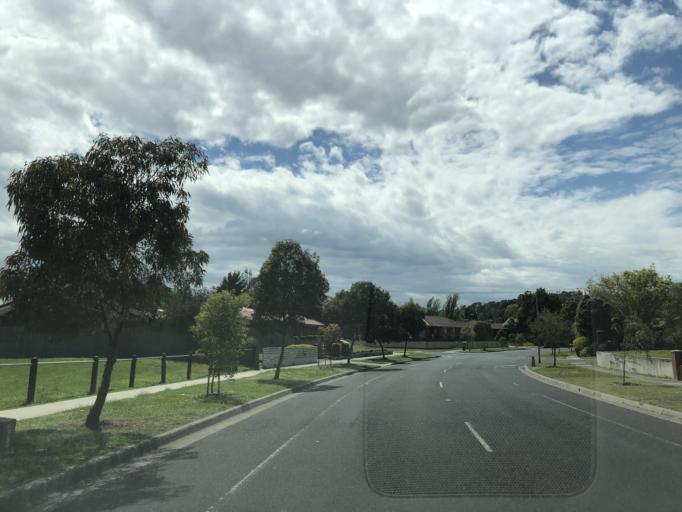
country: AU
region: Victoria
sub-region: Casey
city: Endeavour Hills
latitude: -37.9636
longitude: 145.2637
